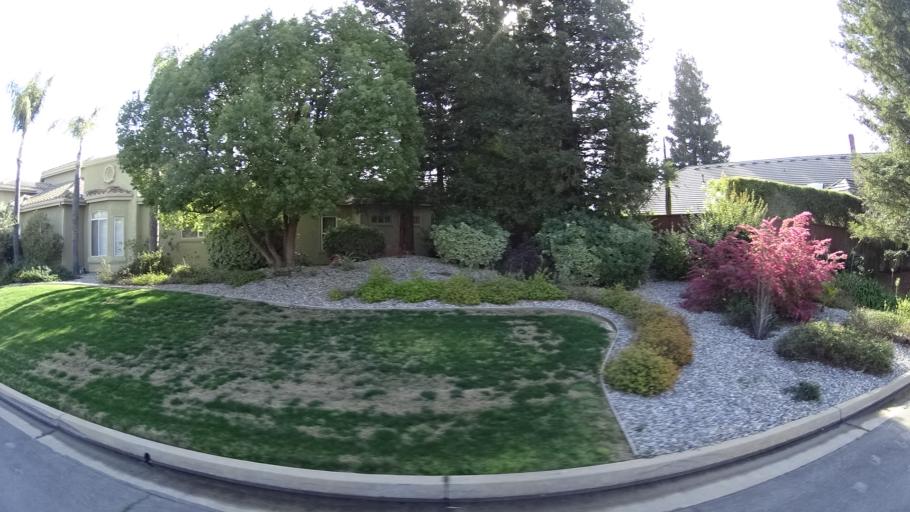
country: US
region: California
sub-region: Fresno County
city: Clovis
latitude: 36.8810
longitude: -119.7676
